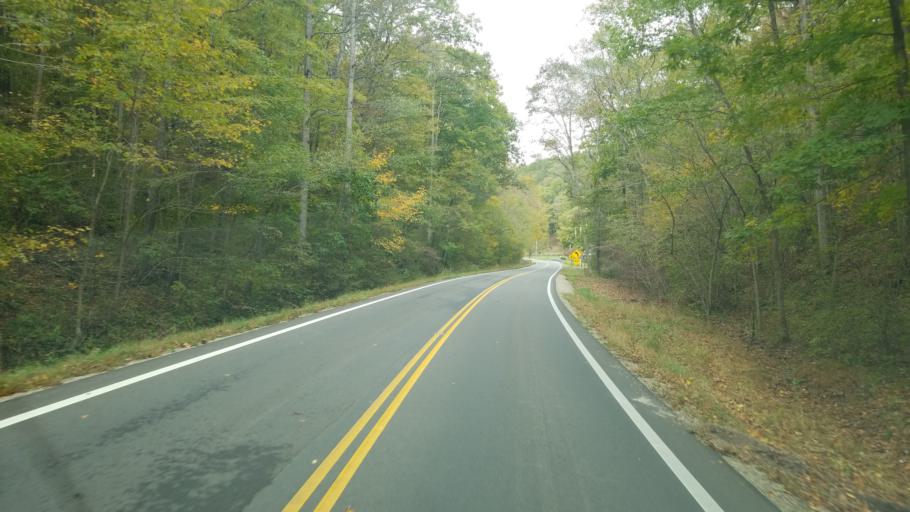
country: US
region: Ohio
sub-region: Jackson County
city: Wellston
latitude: 39.1589
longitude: -82.6181
